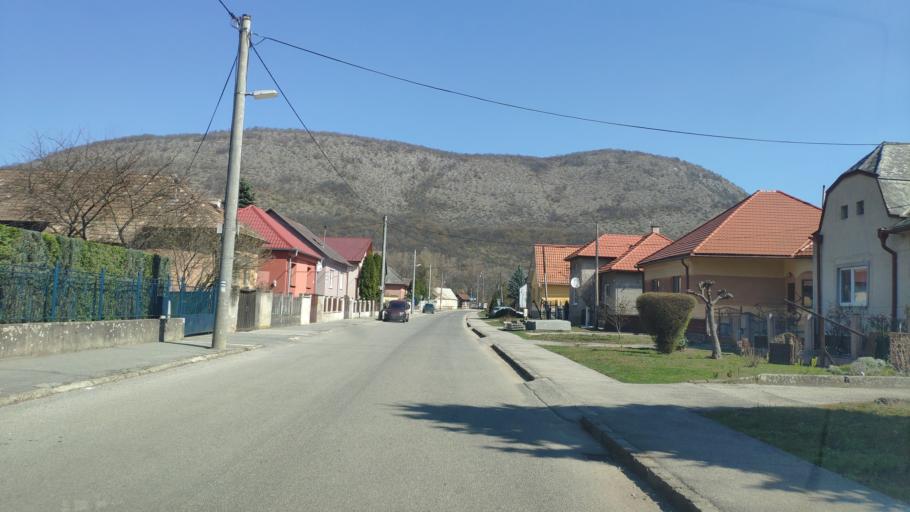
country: SK
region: Kosicky
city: Roznava
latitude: 48.5507
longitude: 20.4059
